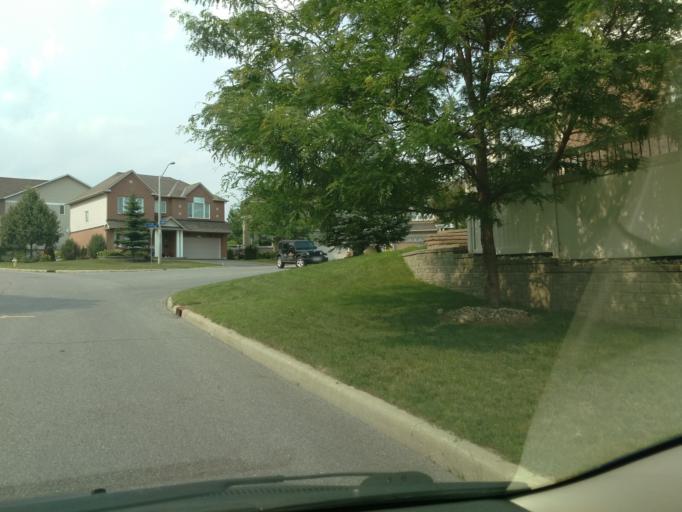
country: CA
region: Quebec
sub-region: Outaouais
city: Gatineau
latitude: 45.4796
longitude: -75.5291
